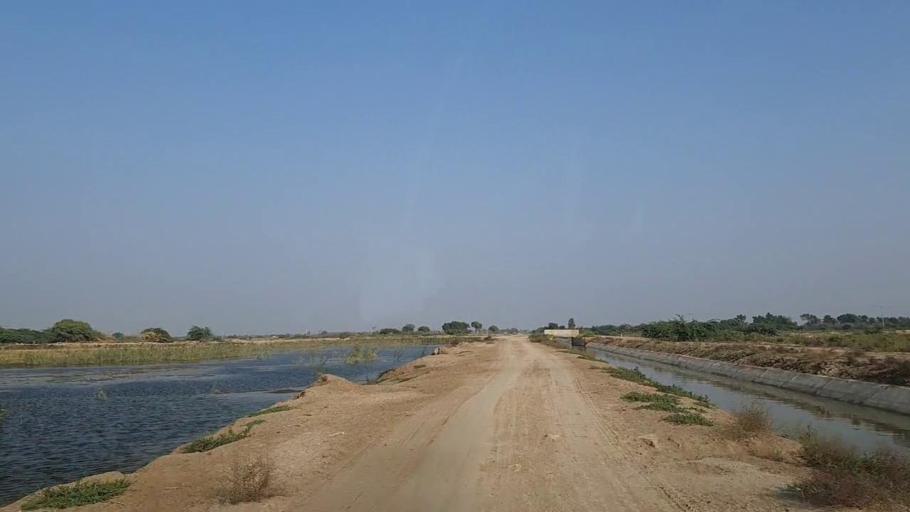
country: PK
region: Sindh
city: Mirpur Sakro
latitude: 24.6154
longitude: 67.7163
